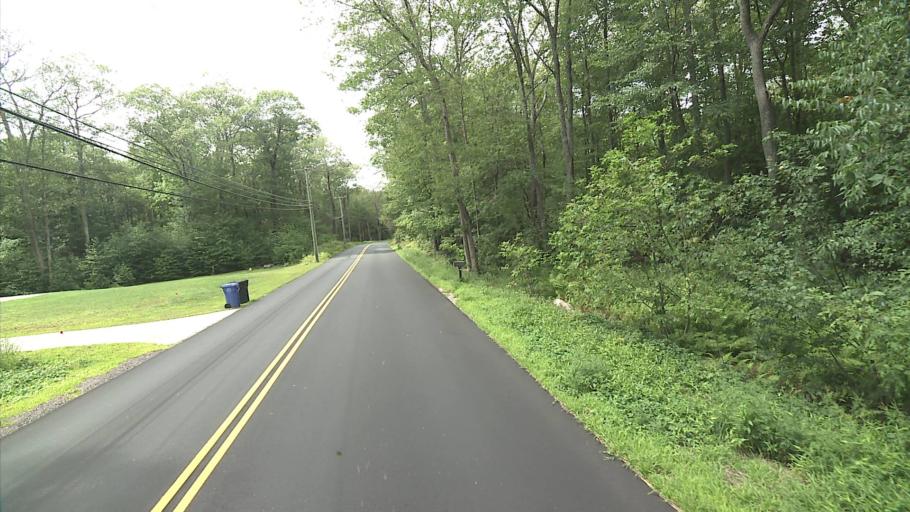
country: US
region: Connecticut
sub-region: Windham County
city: South Woodstock
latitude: 41.9392
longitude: -71.9988
